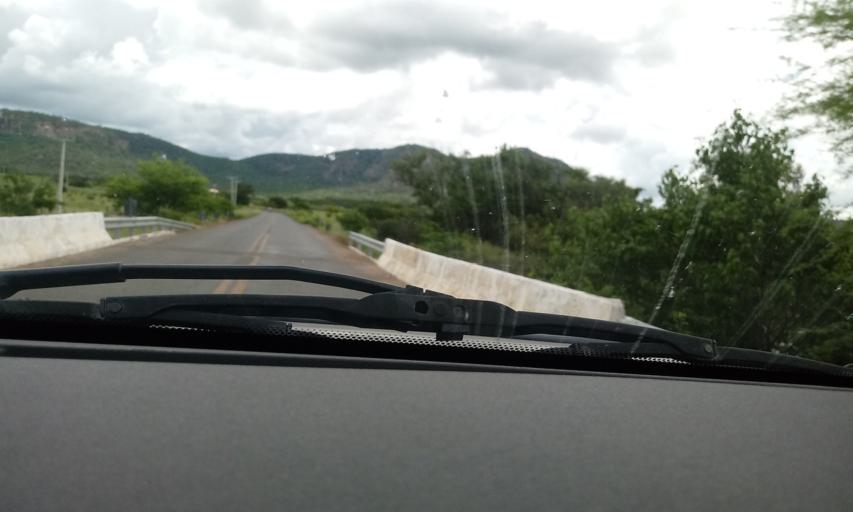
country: BR
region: Bahia
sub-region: Guanambi
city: Guanambi
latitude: -14.1510
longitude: -42.8264
